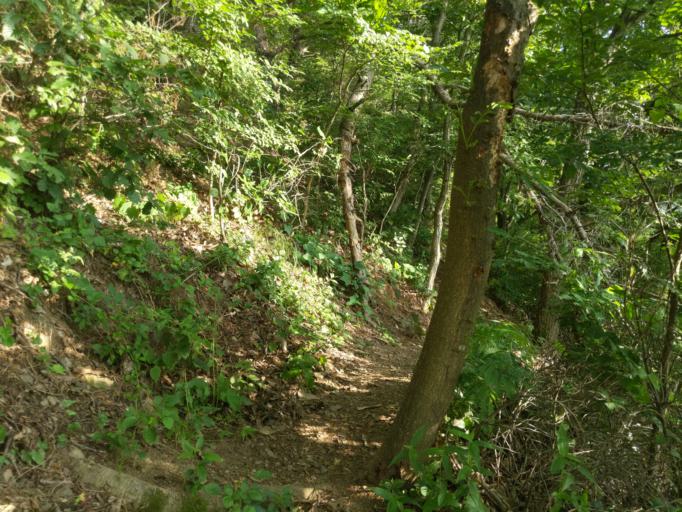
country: KR
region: Daegu
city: Hwawon
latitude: 35.7901
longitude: 128.5406
